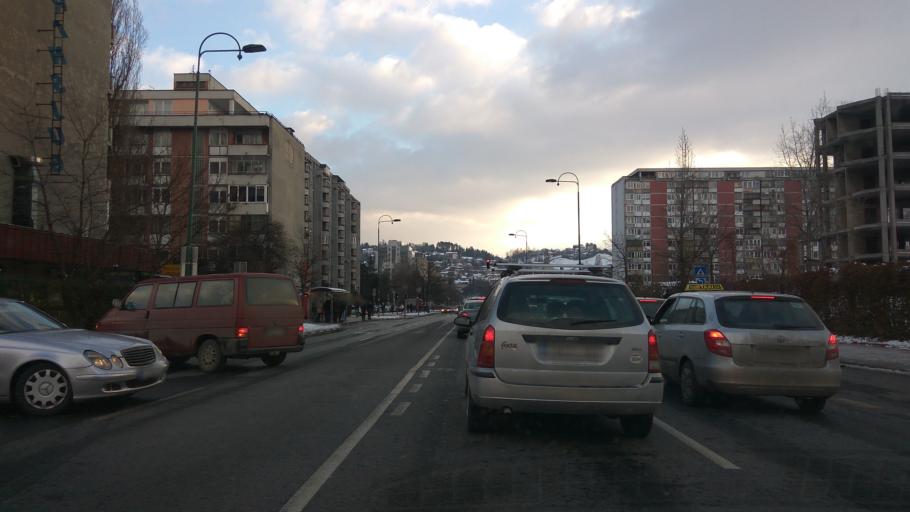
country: BA
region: Federation of Bosnia and Herzegovina
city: Kobilja Glava
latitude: 43.8561
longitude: 18.3918
